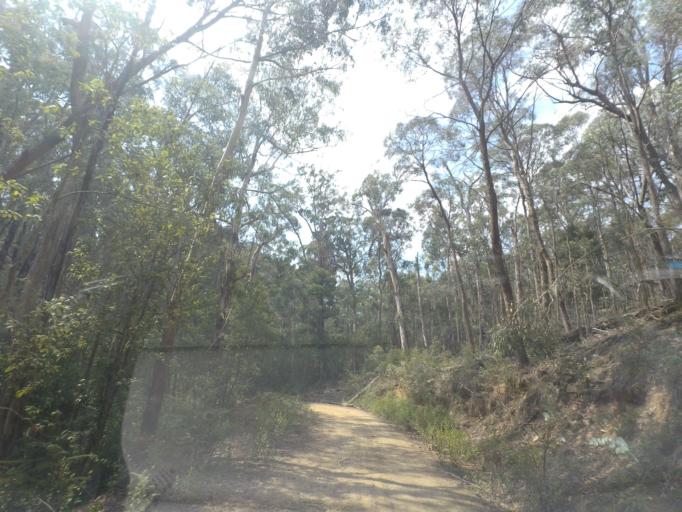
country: AU
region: Victoria
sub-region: Moorabool
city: Bacchus Marsh
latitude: -37.4601
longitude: 144.3819
